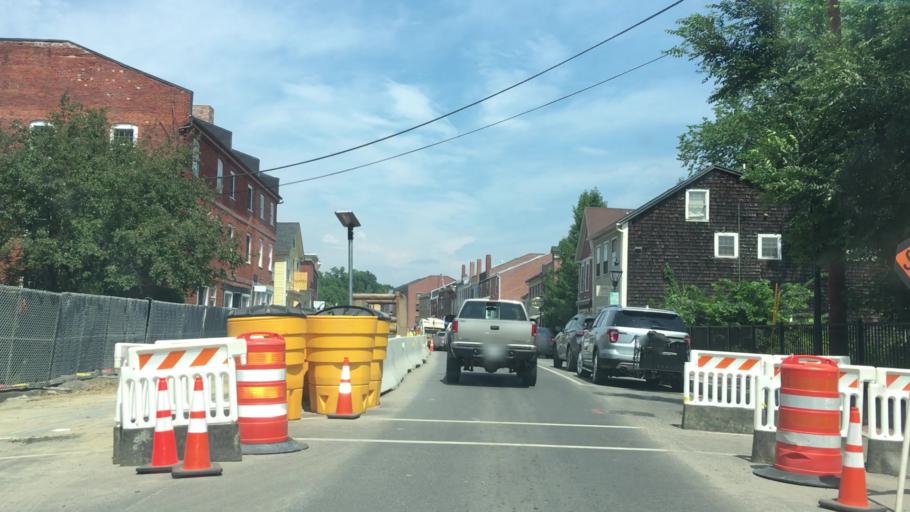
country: US
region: Maine
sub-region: Kennebec County
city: Hallowell
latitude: 44.2844
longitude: -69.7905
